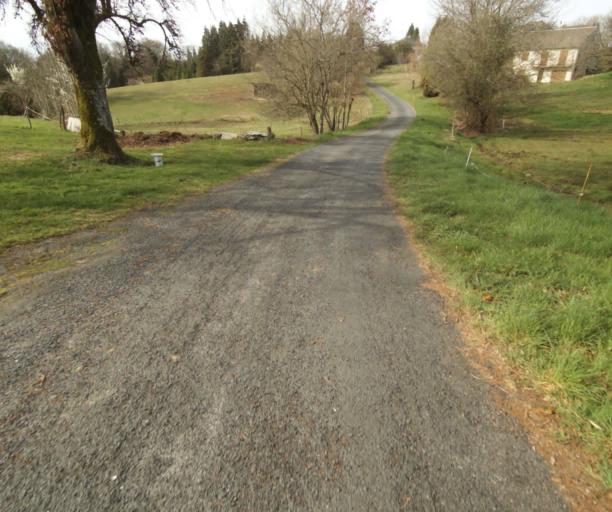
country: FR
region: Limousin
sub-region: Departement de la Correze
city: Correze
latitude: 45.4235
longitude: 1.8351
